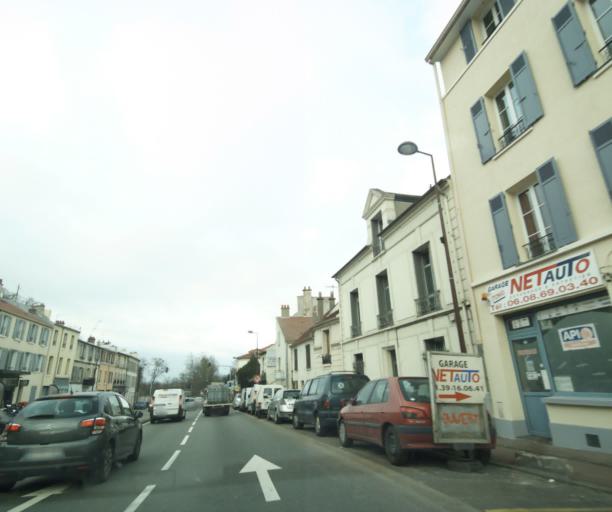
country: FR
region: Ile-de-France
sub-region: Departement des Yvelines
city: Le Port-Marly
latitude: 48.8787
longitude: 2.1084
